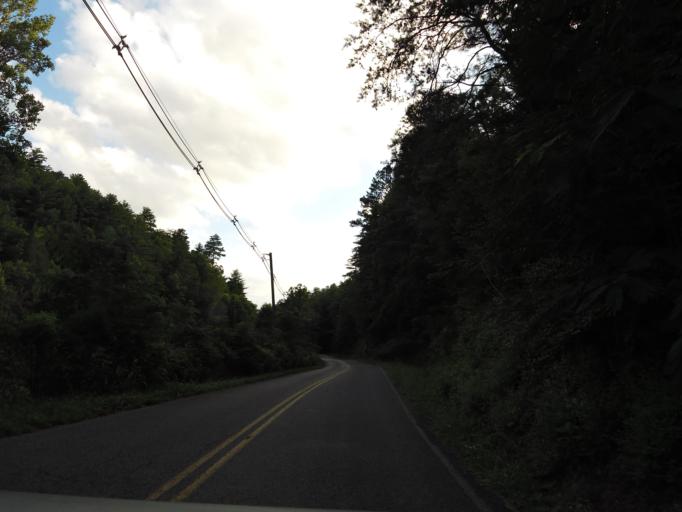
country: US
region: Tennessee
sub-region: Blount County
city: Maryville
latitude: 35.5977
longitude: -83.9738
